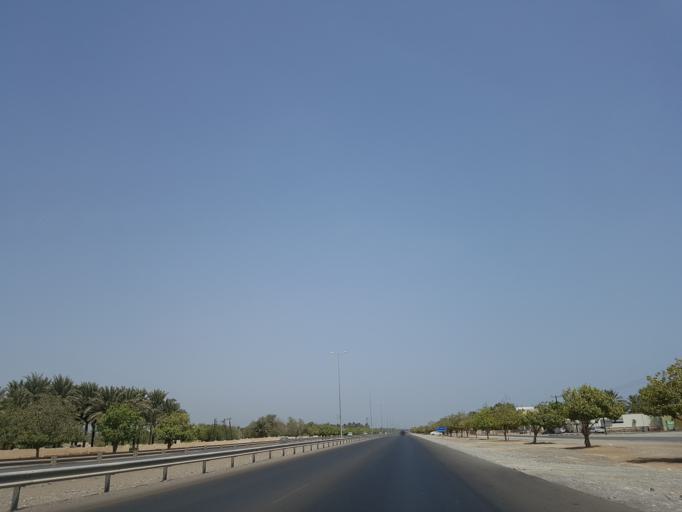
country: OM
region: Al Batinah
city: Saham
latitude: 24.1655
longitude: 56.8625
